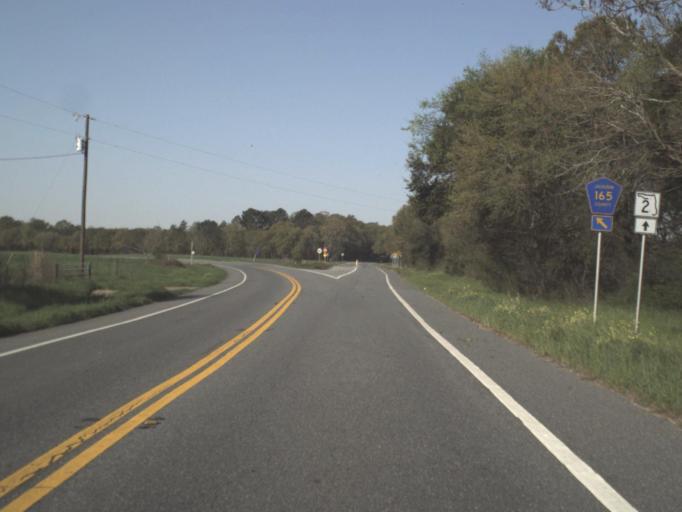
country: US
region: Florida
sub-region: Jackson County
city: Malone
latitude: 30.9646
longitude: -85.1138
